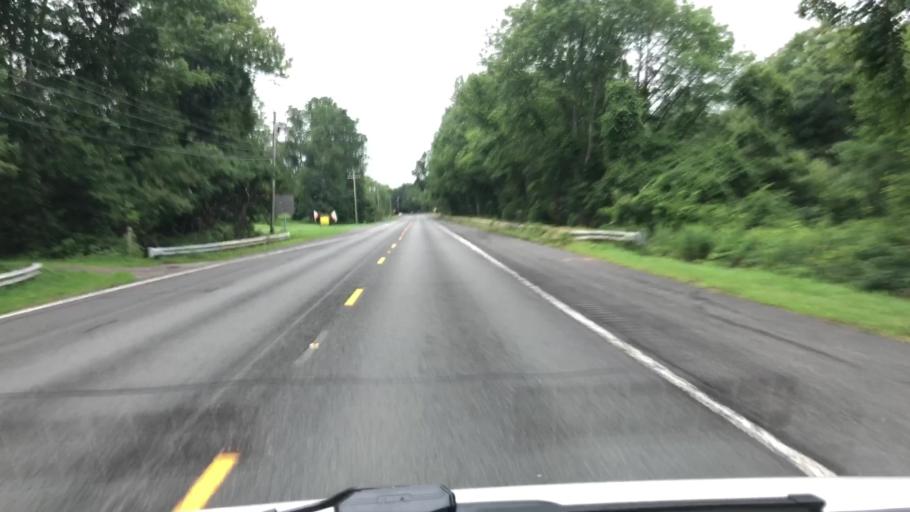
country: US
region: Massachusetts
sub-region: Berkshire County
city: Lanesborough
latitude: 42.5747
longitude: -73.2495
